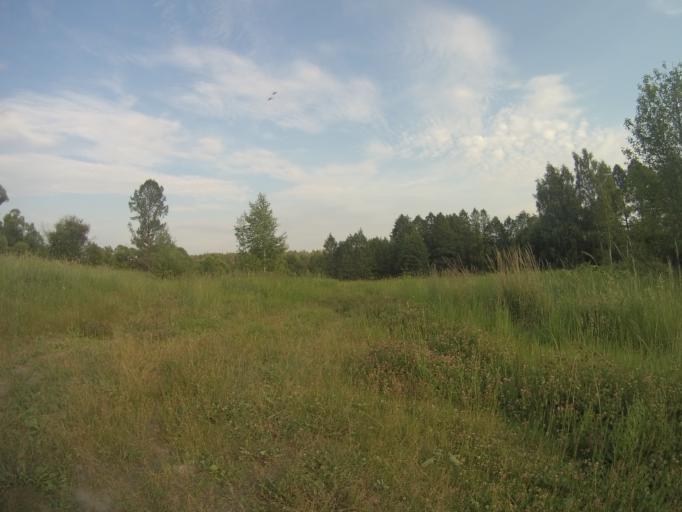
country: RU
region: Vladimir
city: Orgtrud
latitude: 56.0895
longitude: 40.6036
